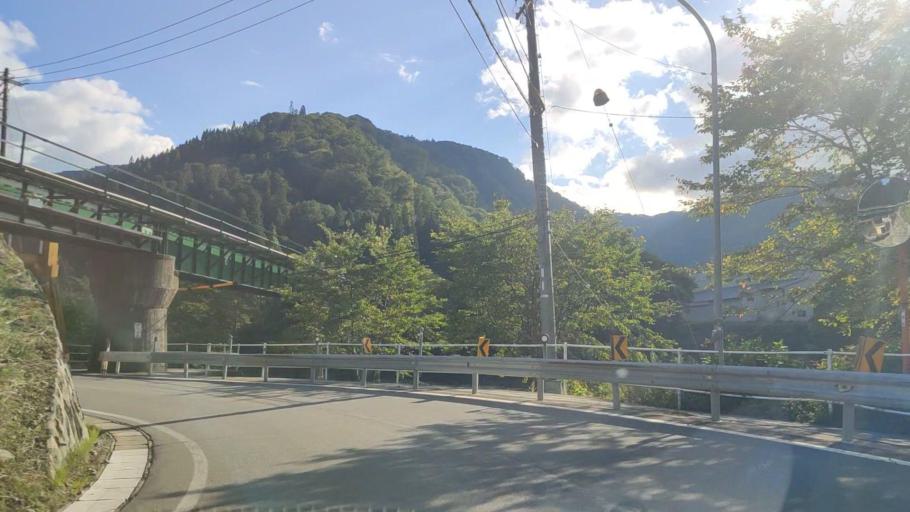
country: JP
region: Gifu
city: Takayama
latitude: 36.3067
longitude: 137.1098
